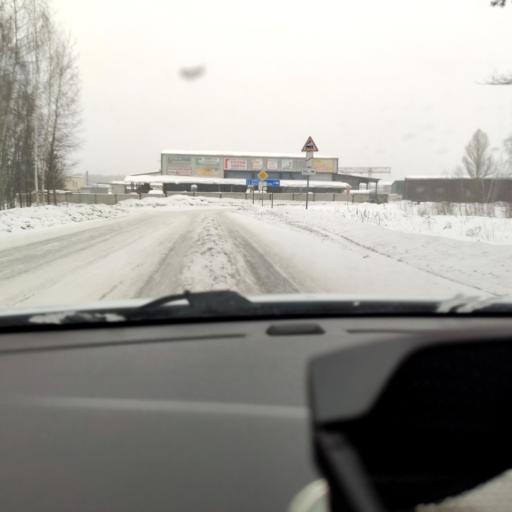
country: RU
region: Tatarstan
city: Vysokaya Gora
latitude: 55.9070
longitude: 49.2702
